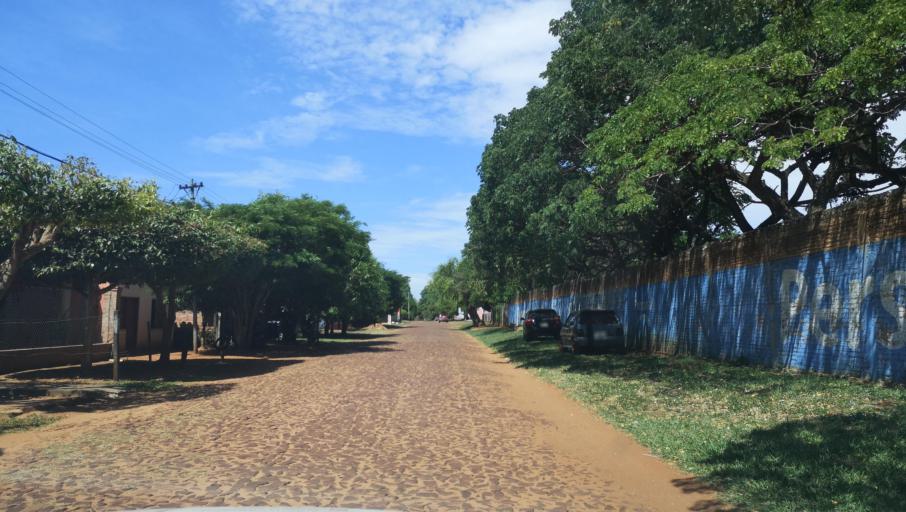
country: PY
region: Misiones
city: Santa Maria
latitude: -26.8962
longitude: -57.0289
